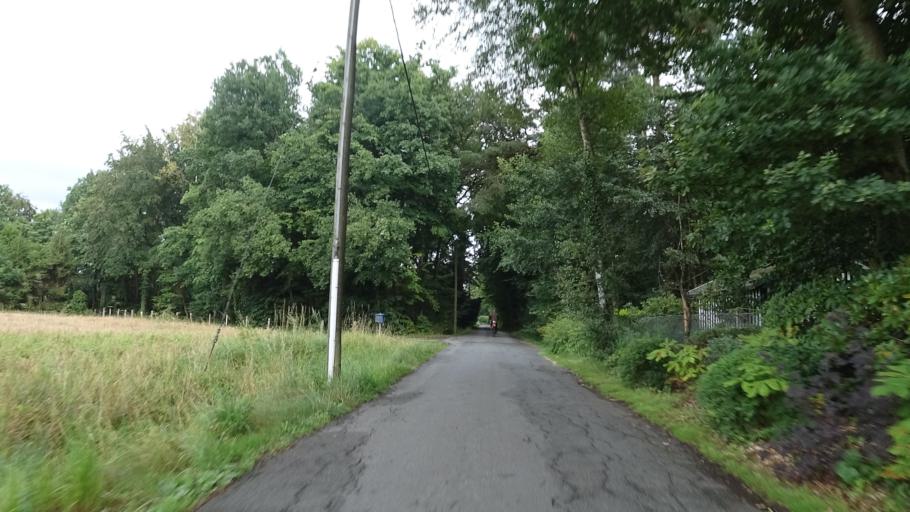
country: DE
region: North Rhine-Westphalia
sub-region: Regierungsbezirk Detmold
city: Guetersloh
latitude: 51.9376
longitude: 8.4072
